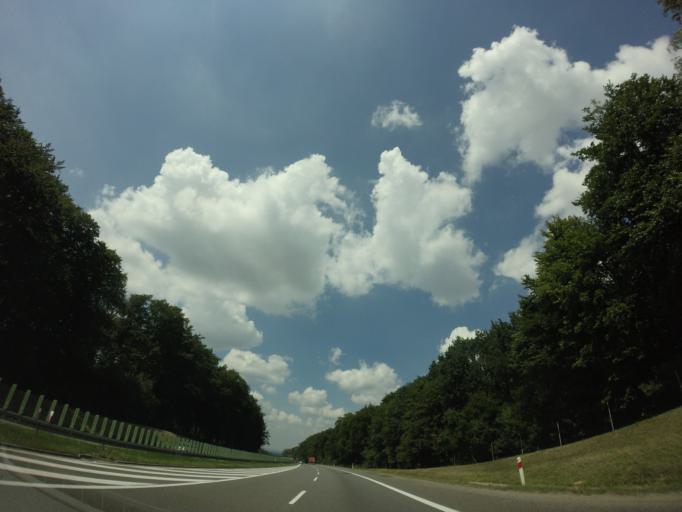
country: PL
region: Opole Voivodeship
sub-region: Powiat krapkowicki
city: Zdzieszowice
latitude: 50.4673
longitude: 18.1505
